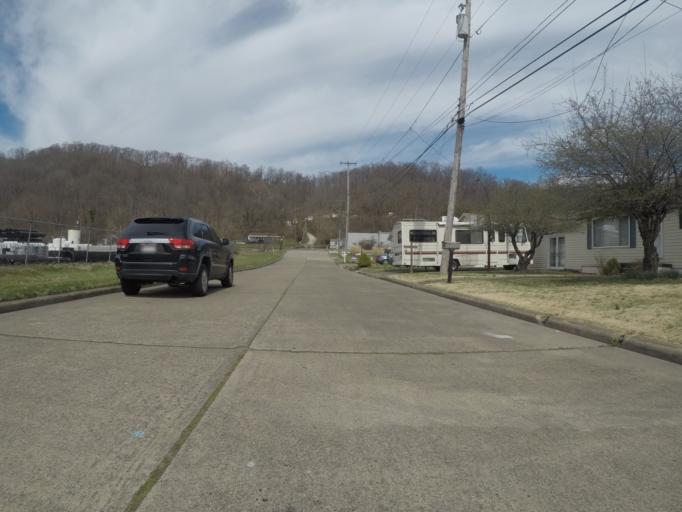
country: US
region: West Virginia
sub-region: Cabell County
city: Pea Ridge
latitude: 38.4166
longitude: -82.3681
